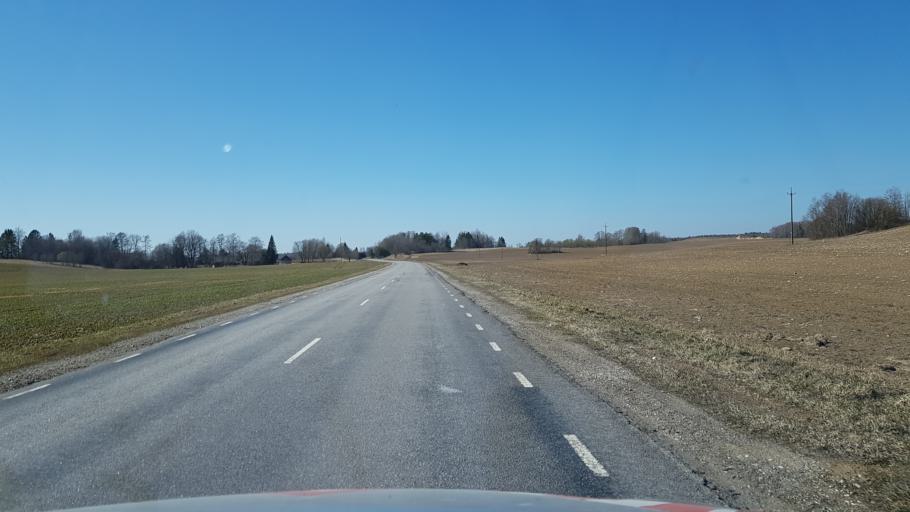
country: EE
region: Laeaene-Virumaa
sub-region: Tamsalu vald
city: Tamsalu
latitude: 59.1670
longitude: 26.1713
